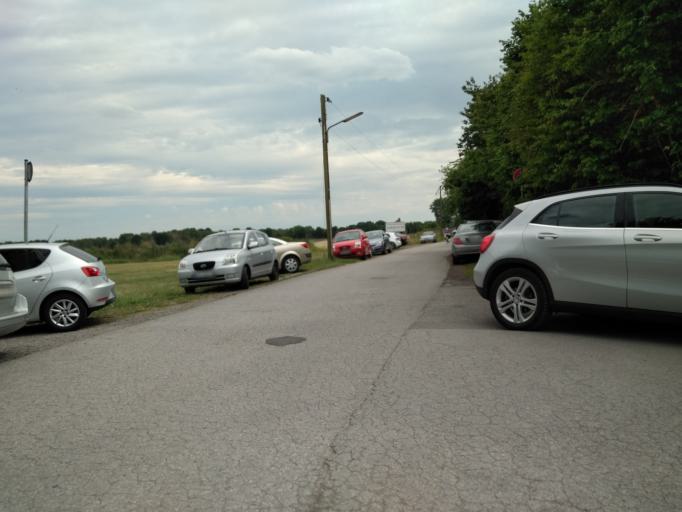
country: DE
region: North Rhine-Westphalia
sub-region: Regierungsbezirk Dusseldorf
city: Schermbeck
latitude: 51.6148
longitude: 6.8634
